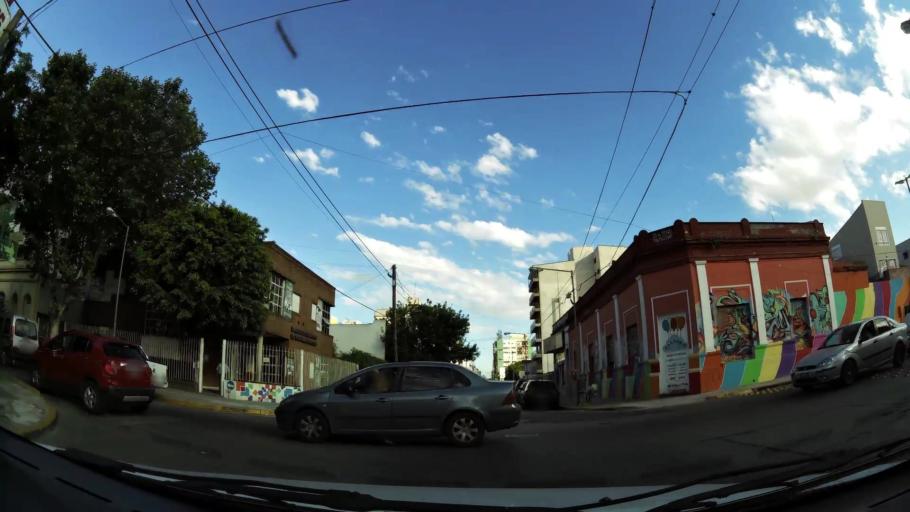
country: AR
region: Buenos Aires
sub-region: Partido de General San Martin
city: General San Martin
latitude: -34.5483
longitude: -58.5575
